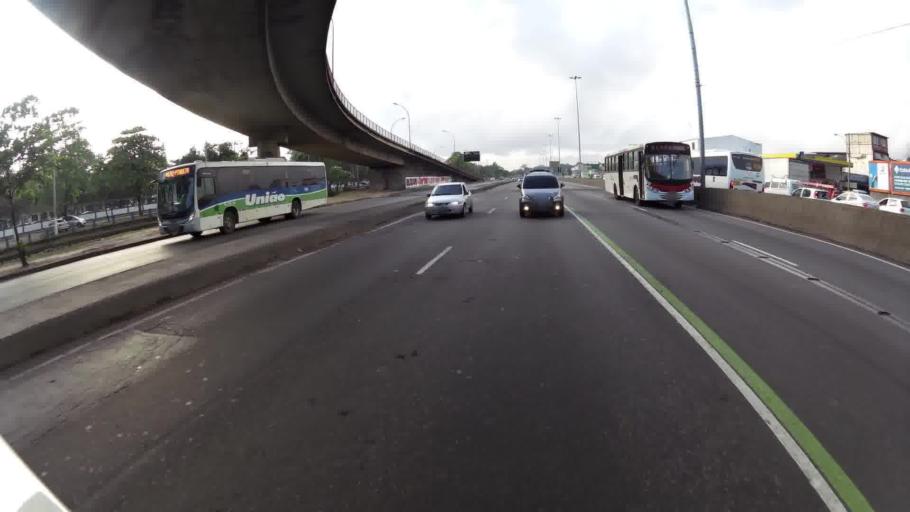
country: BR
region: Rio de Janeiro
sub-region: Duque De Caxias
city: Duque de Caxias
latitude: -22.8269
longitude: -43.2746
